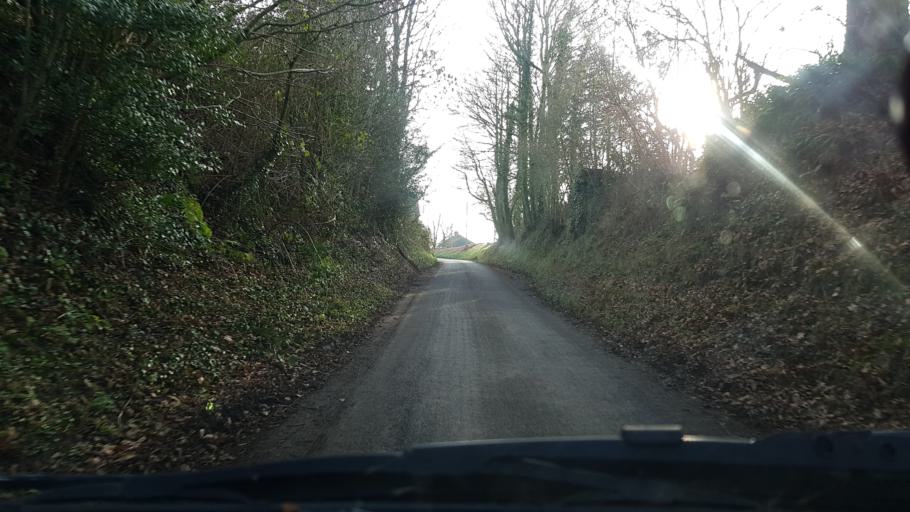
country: GB
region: England
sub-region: Wiltshire
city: Burbage
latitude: 51.3613
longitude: -1.7177
